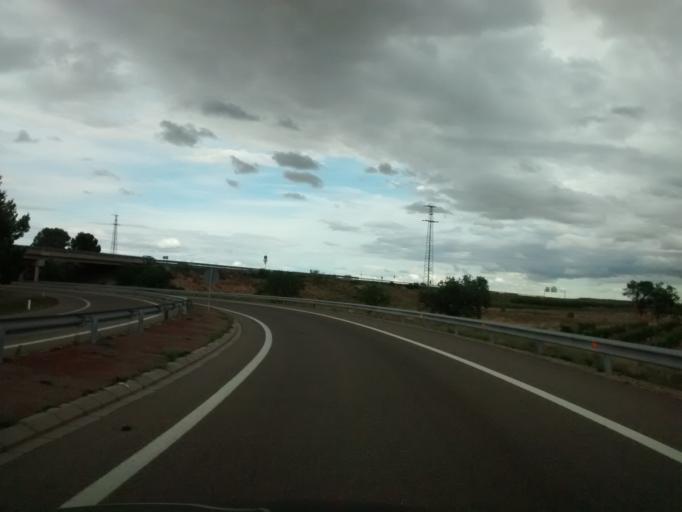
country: ES
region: Navarre
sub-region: Provincia de Navarra
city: Murchante
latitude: 42.0298
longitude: -1.6337
